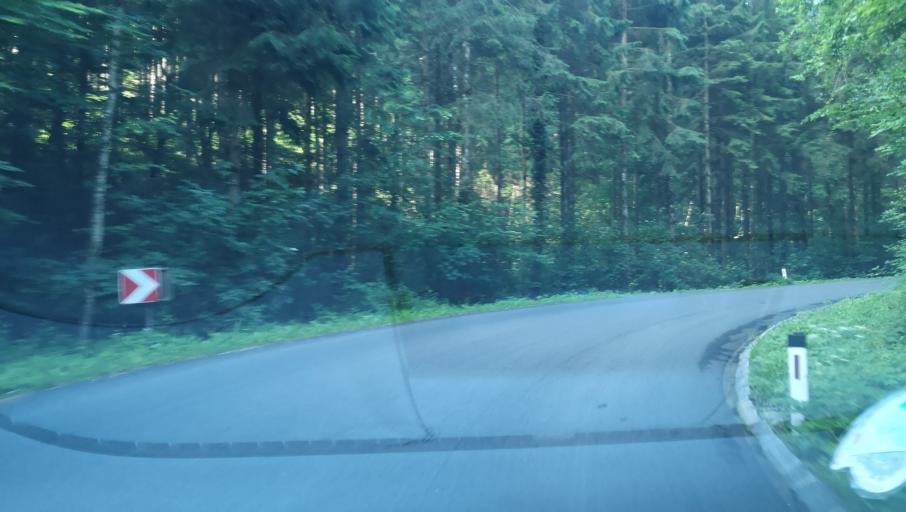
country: AT
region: Lower Austria
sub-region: Politischer Bezirk Scheibbs
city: Wang
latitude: 48.0153
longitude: 15.0396
